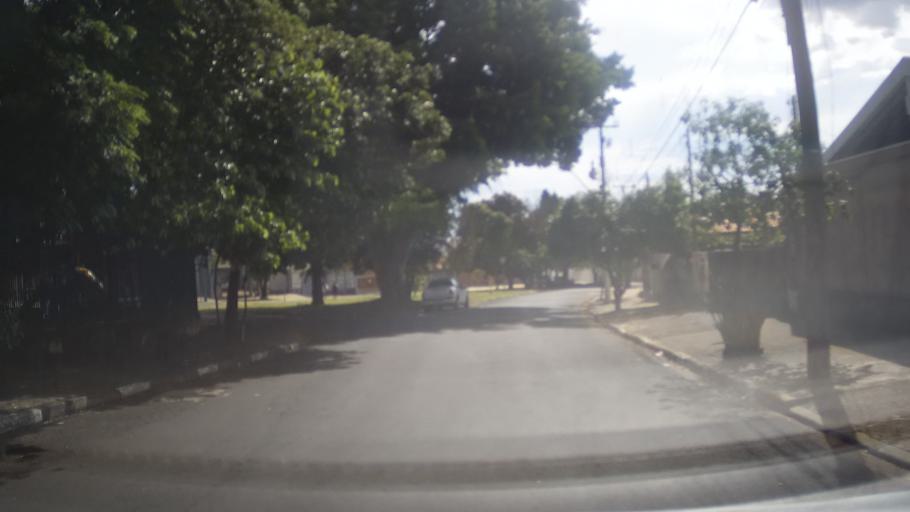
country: BR
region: Sao Paulo
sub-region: Campinas
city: Campinas
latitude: -22.8869
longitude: -47.1103
